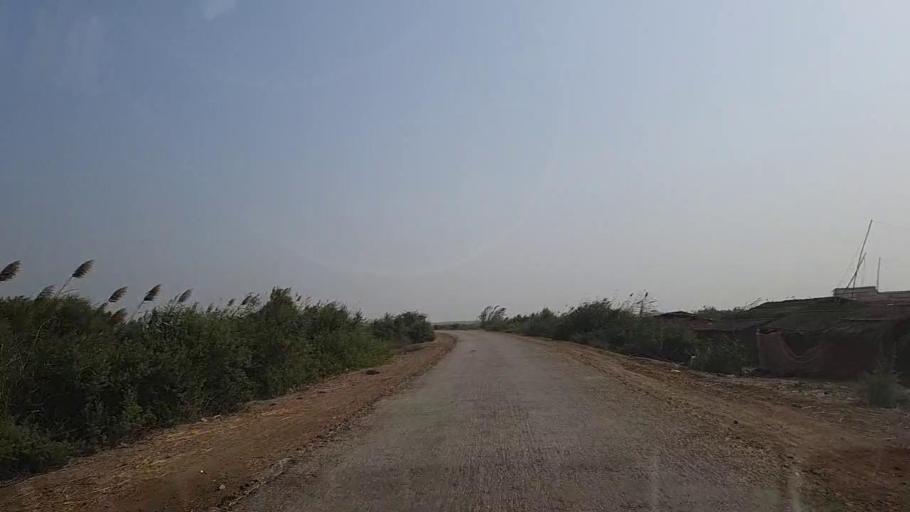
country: PK
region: Sindh
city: Keti Bandar
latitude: 24.2344
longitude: 67.6429
